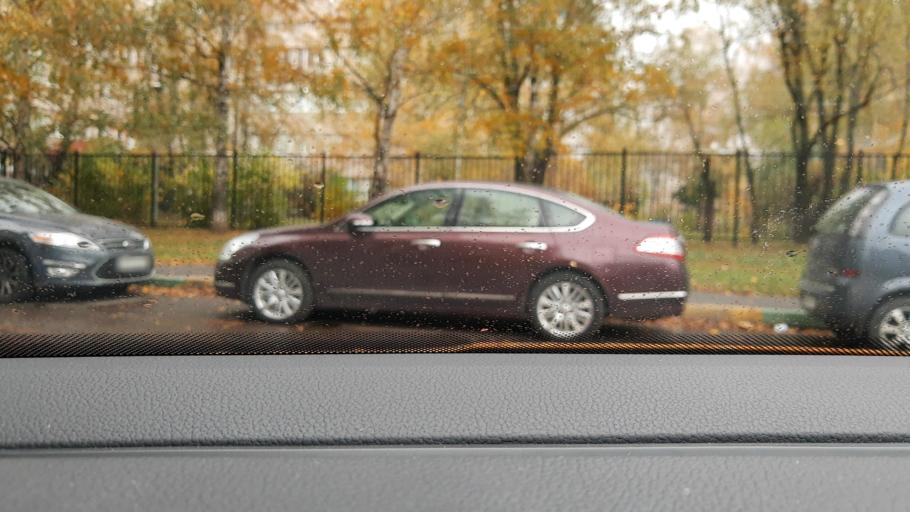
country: RU
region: Moscow
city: Strogino
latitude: 55.7966
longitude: 37.3953
